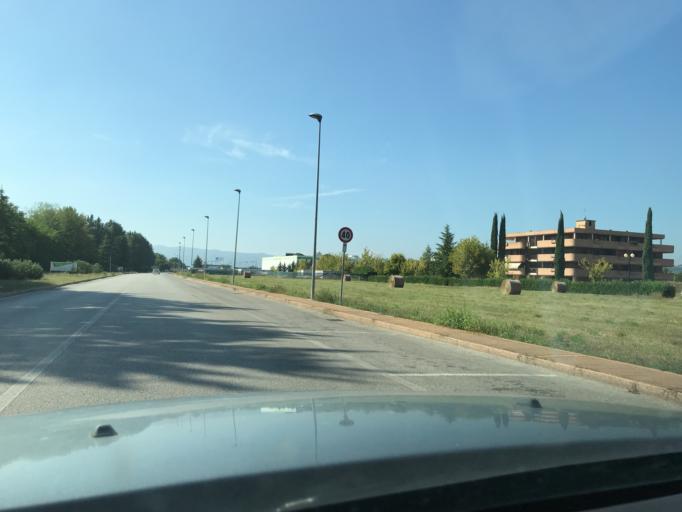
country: IT
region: Umbria
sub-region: Provincia di Perugia
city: Ospedalicchio
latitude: 43.0782
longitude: 12.5098
